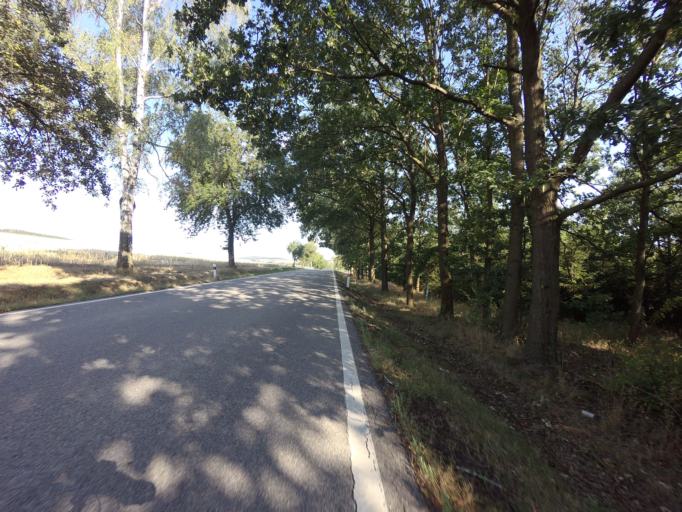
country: CZ
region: Jihocesky
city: Tyn nad Vltavou
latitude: 49.2707
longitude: 14.4067
